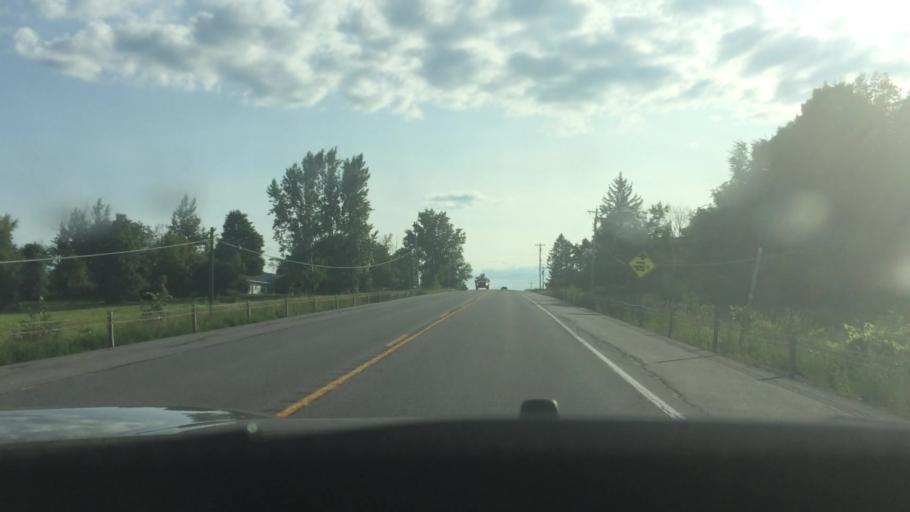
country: US
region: New York
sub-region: St. Lawrence County
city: Canton
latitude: 44.6231
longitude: -75.0975
